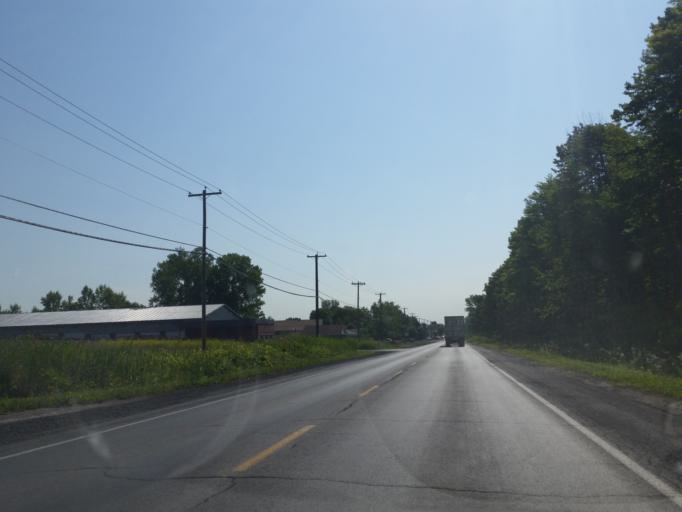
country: CA
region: Quebec
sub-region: Monteregie
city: Saint-Jean-sur-Richelieu
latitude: 45.3036
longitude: -73.3062
